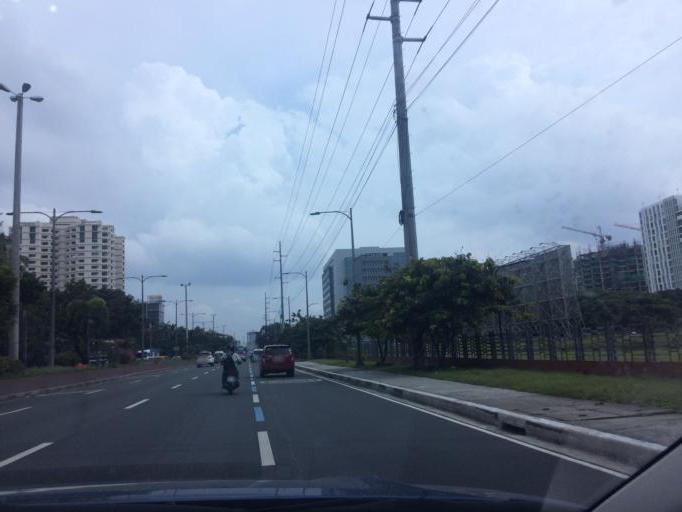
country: PH
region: Metro Manila
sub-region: Makati City
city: Makati City
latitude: 14.5433
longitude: 120.9915
